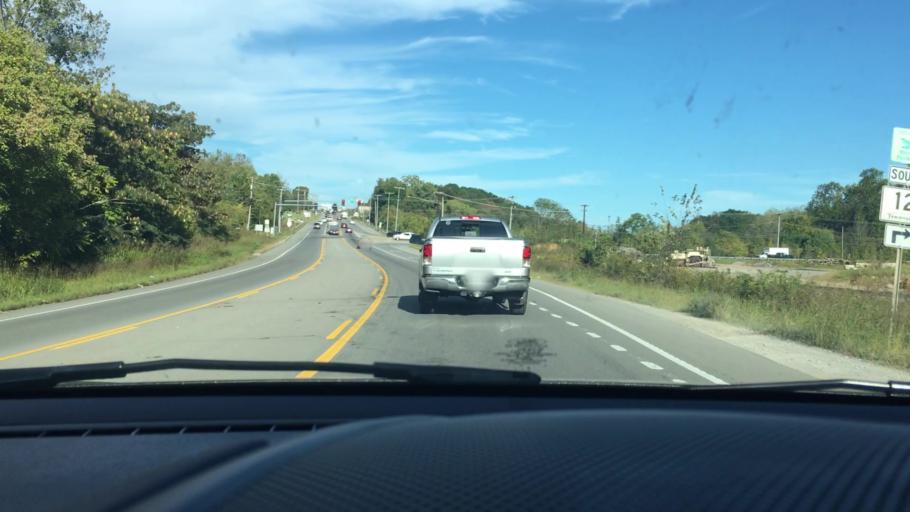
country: US
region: Tennessee
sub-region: Montgomery County
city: Clarksville
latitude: 36.5001
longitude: -87.2920
